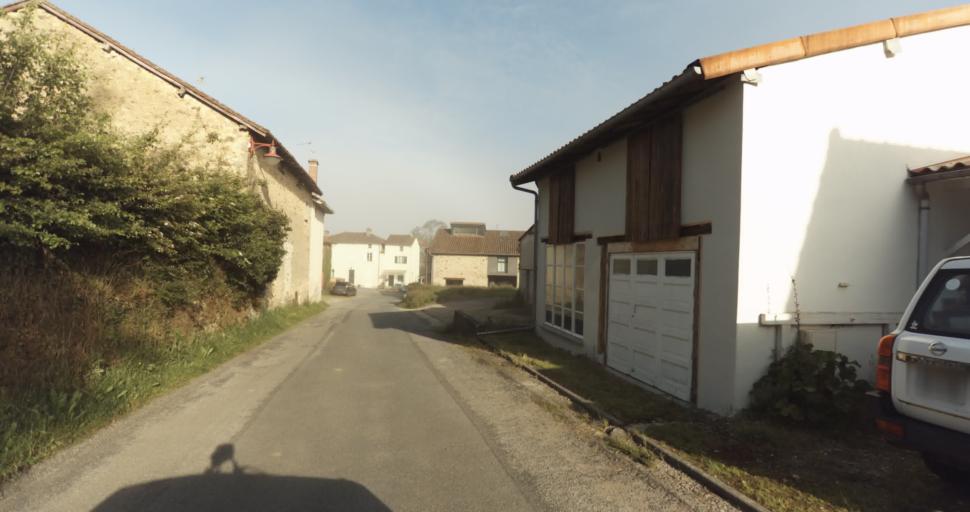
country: FR
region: Limousin
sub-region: Departement de la Haute-Vienne
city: Condat-sur-Vienne
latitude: 45.7824
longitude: 1.2806
